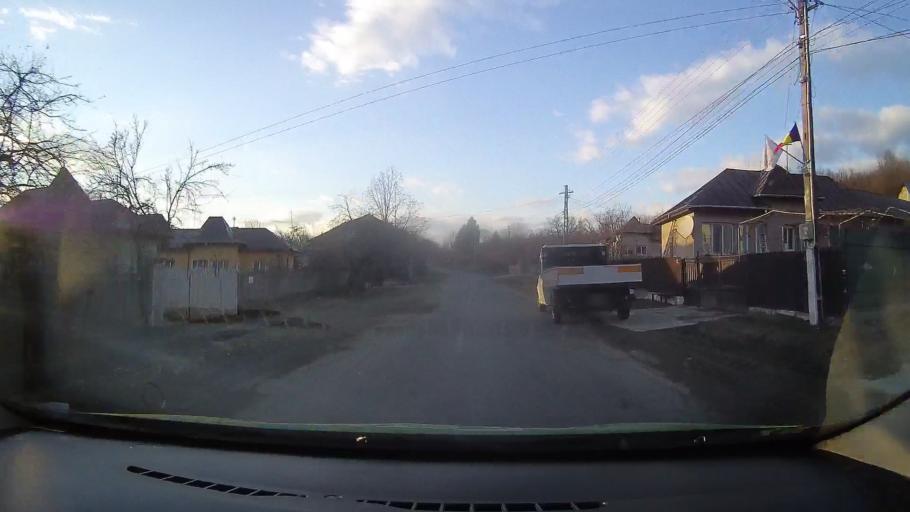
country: RO
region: Dambovita
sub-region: Comuna Gura Ocnitei
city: Adanca
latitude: 44.9191
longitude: 25.6162
